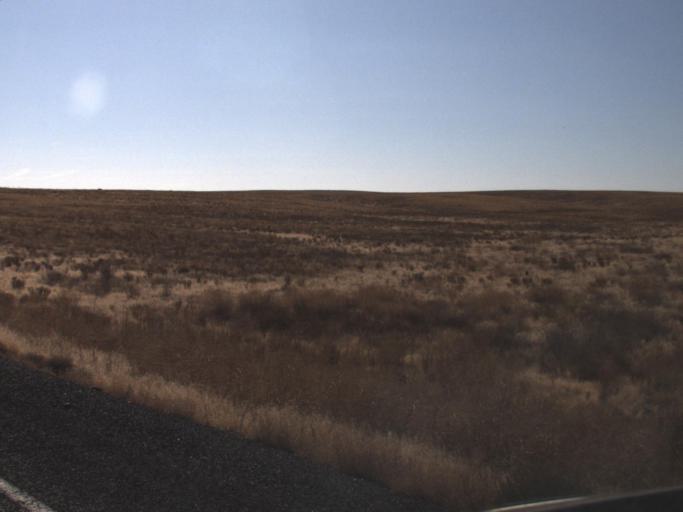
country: US
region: Washington
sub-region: Franklin County
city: Connell
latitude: 46.7196
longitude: -118.5481
